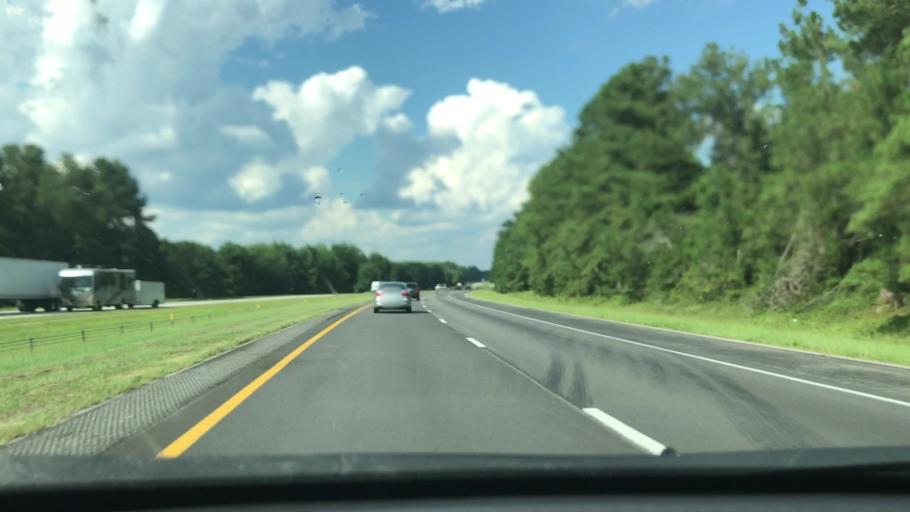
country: US
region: South Carolina
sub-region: Clarendon County
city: Manning
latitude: 33.8084
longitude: -80.1565
